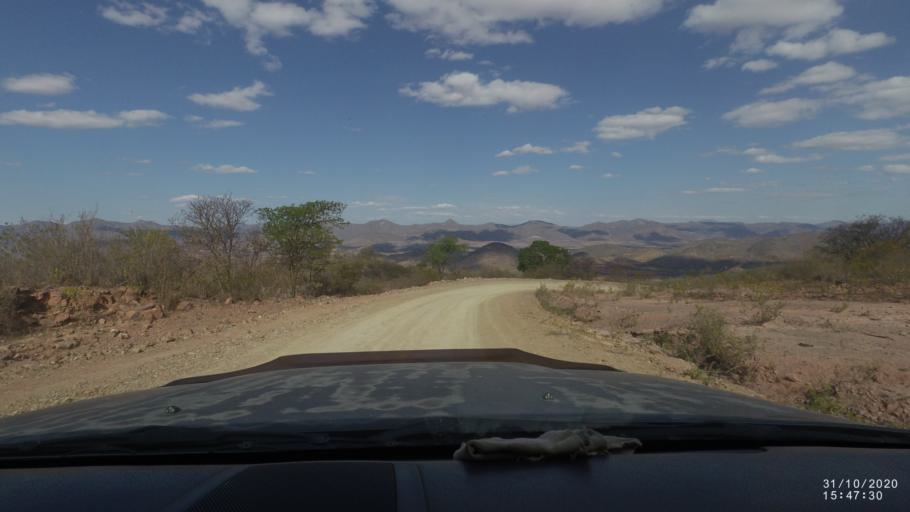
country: BO
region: Chuquisaca
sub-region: Provincia Zudanez
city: Mojocoya
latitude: -18.3134
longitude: -64.7139
